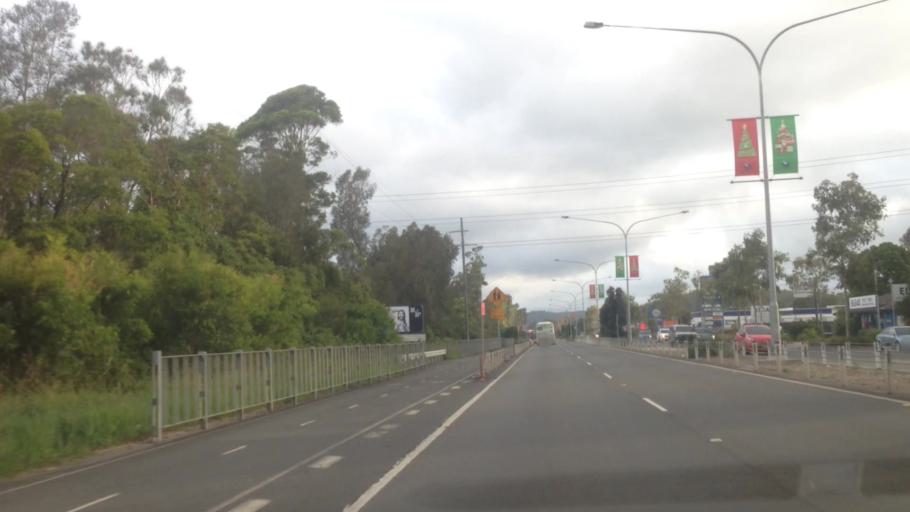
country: AU
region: New South Wales
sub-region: Wyong Shire
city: Chittaway Bay
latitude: -33.2985
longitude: 151.4219
